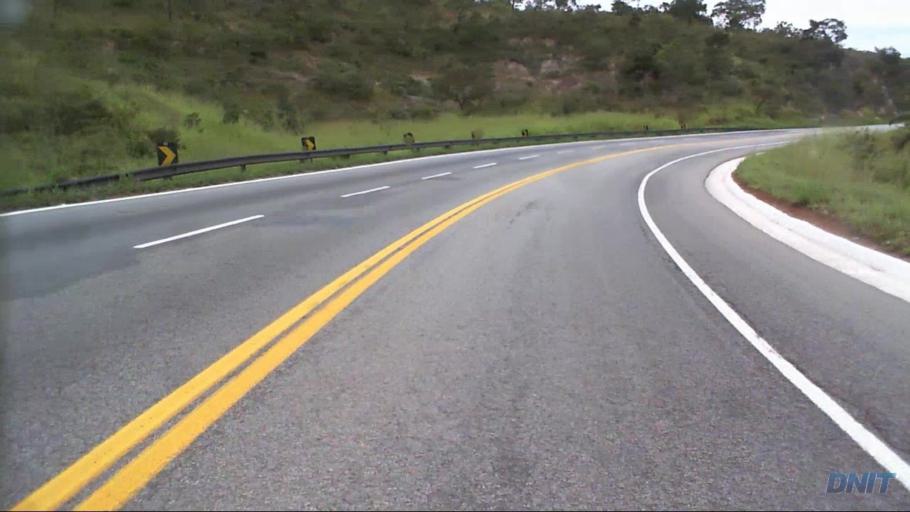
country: BR
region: Minas Gerais
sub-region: Caete
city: Caete
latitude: -19.7889
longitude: -43.7044
